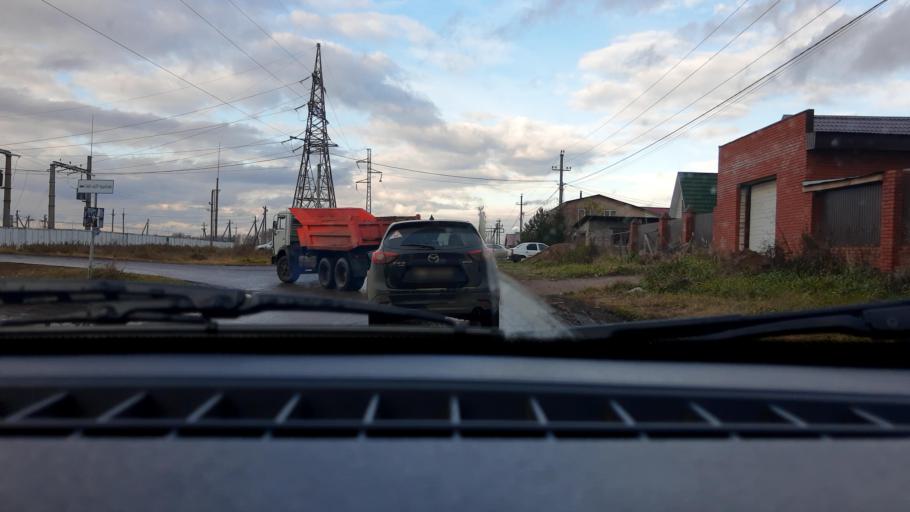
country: RU
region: Bashkortostan
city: Ufa
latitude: 54.8424
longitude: 55.9993
